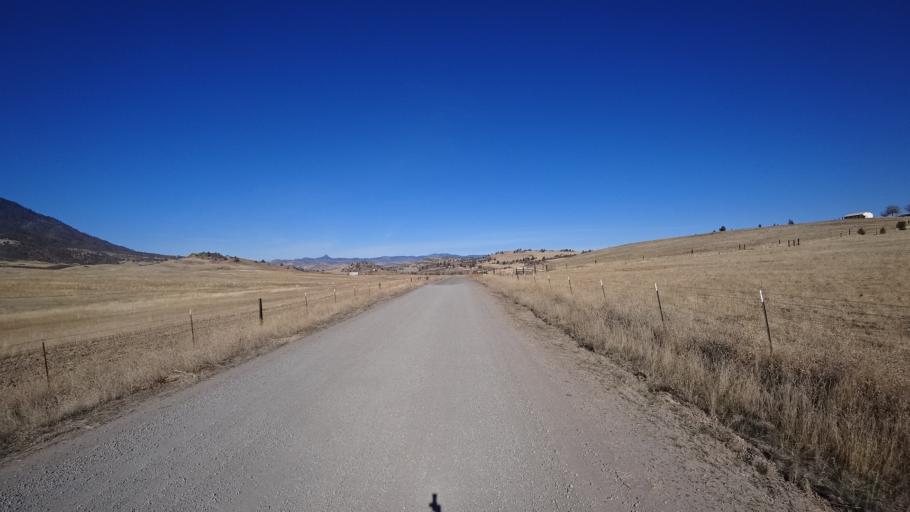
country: US
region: California
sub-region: Siskiyou County
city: Montague
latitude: 41.8435
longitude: -122.4596
